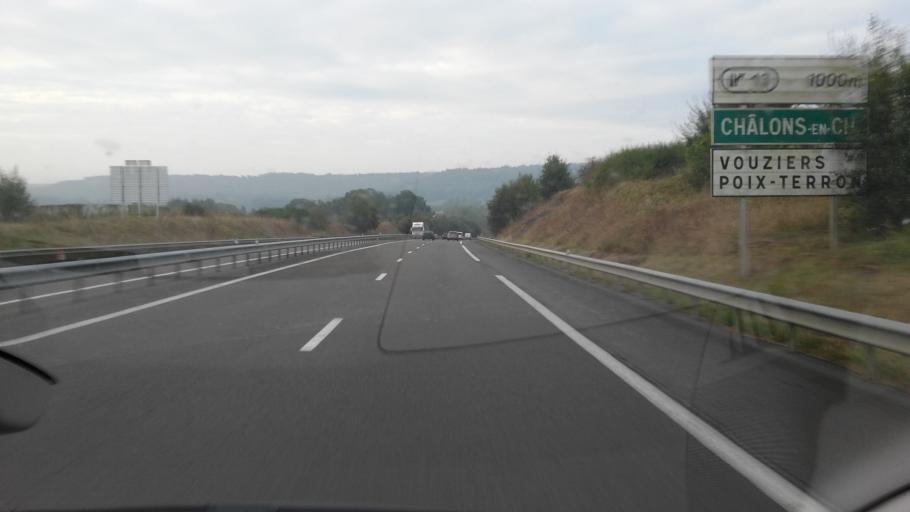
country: FR
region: Champagne-Ardenne
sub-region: Departement des Ardennes
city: La Francheville
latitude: 49.6537
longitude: 4.6342
